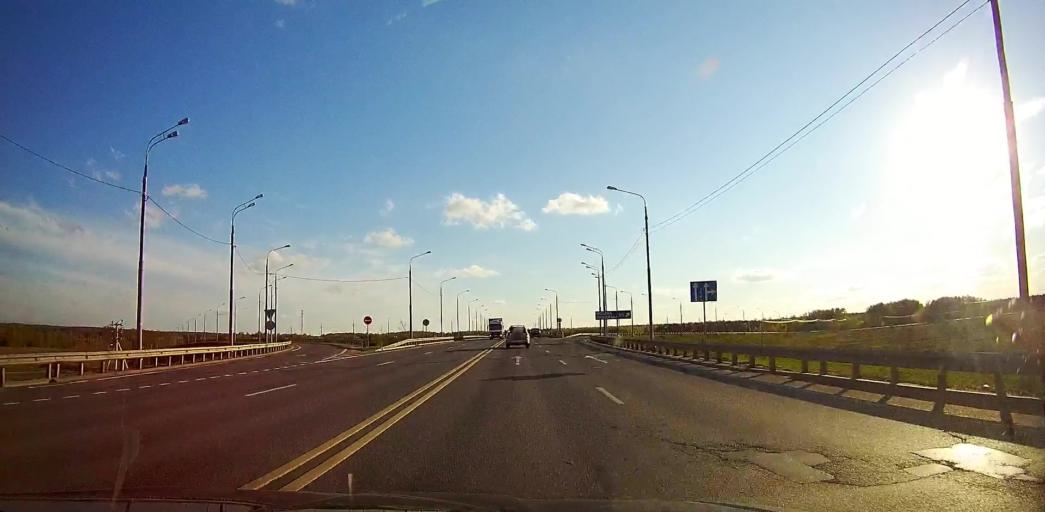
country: RU
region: Moskovskaya
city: Bronnitsy
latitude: 55.4130
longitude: 38.2410
